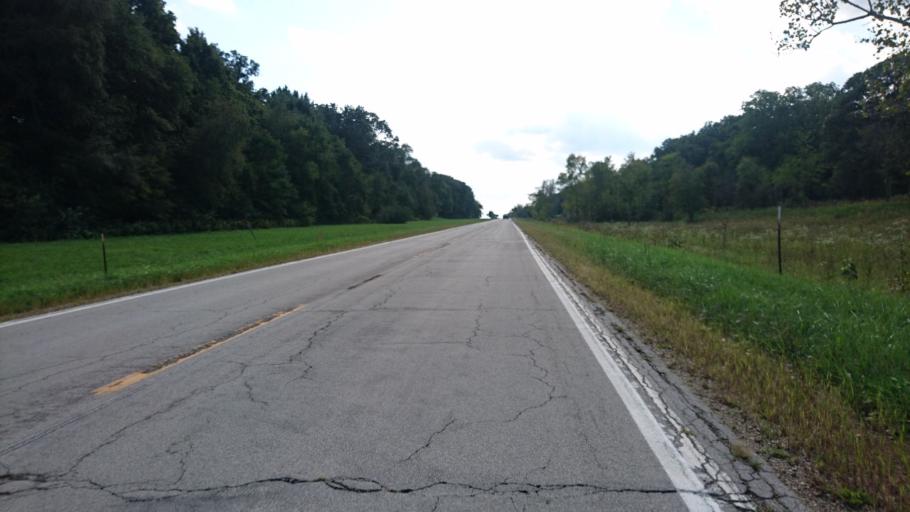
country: US
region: Illinois
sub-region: McLean County
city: Twin Grove
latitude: 40.3595
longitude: -89.1165
